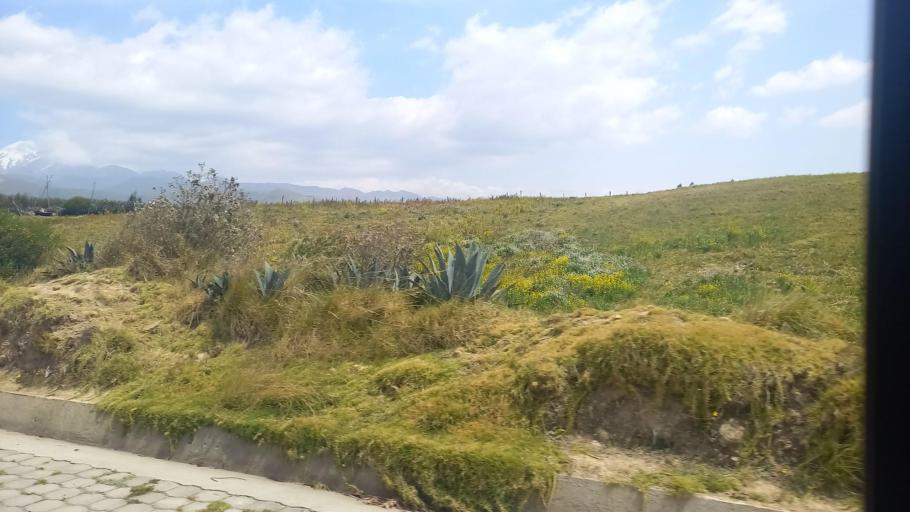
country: EC
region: Pichincha
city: Cayambe
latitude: 0.1592
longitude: -78.0758
